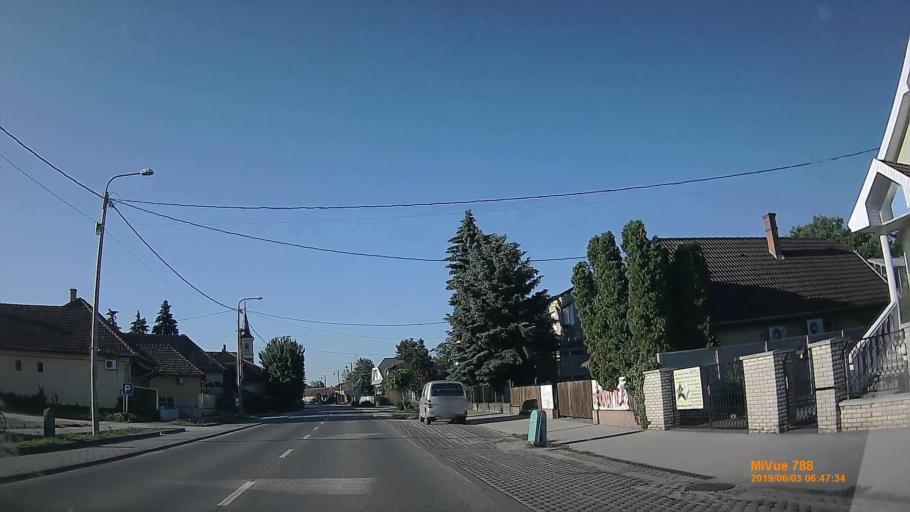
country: HU
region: Pest
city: Bugyi
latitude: 47.2250
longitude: 19.1492
